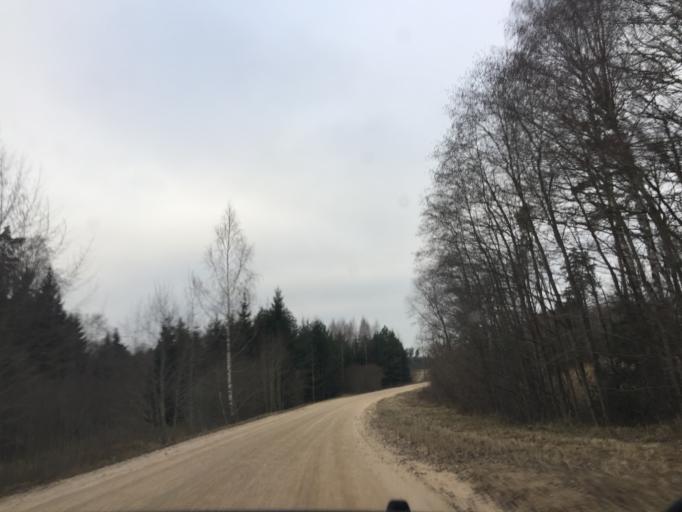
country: LV
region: Ligatne
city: Ligatne
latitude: 57.2091
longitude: 25.1361
